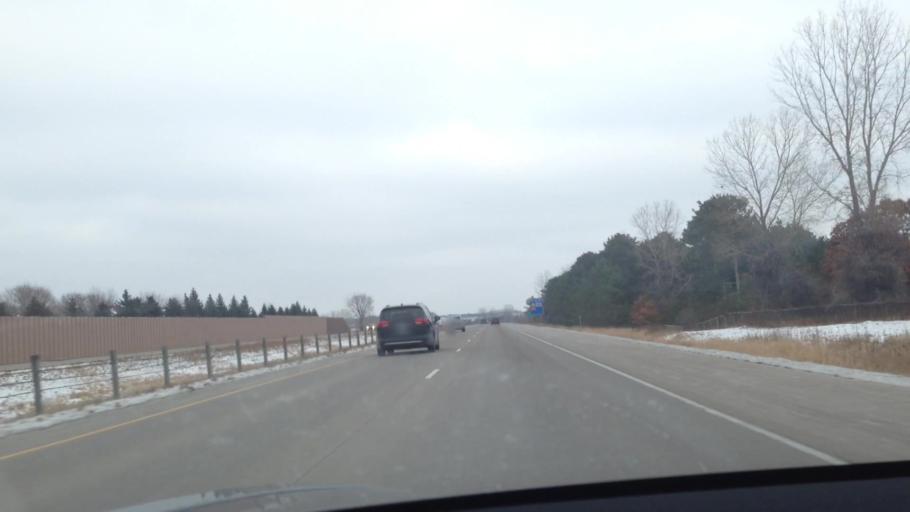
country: US
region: Minnesota
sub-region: Anoka County
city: Circle Pines
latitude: 45.1691
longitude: -93.1371
